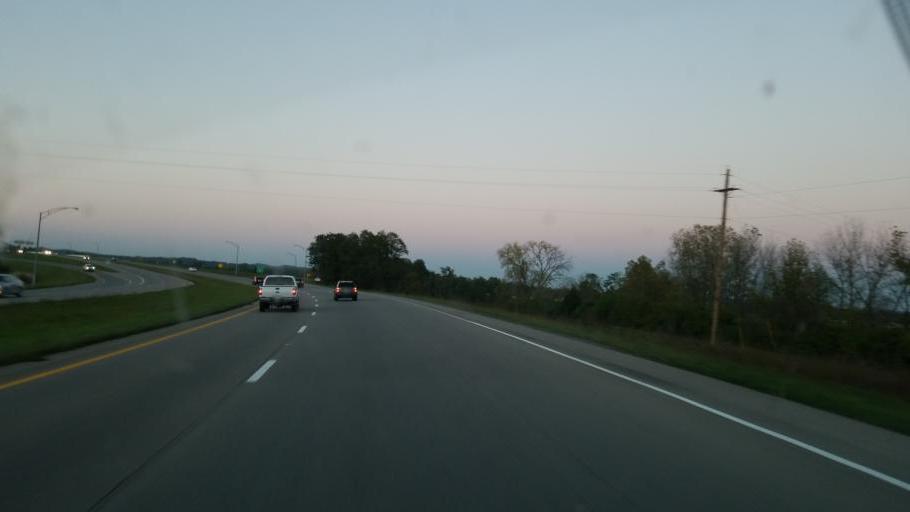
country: US
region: Ohio
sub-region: Ross County
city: Chillicothe
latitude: 39.2868
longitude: -82.9476
